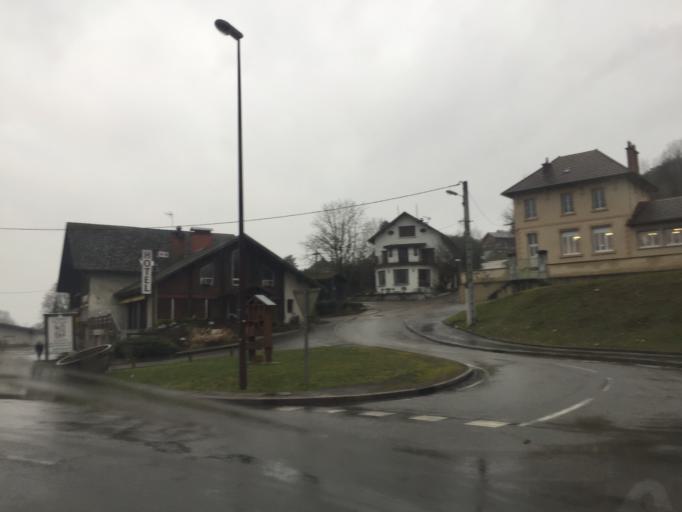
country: FR
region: Franche-Comte
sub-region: Departement du Jura
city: Mouchard
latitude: 46.9781
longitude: 5.8070
